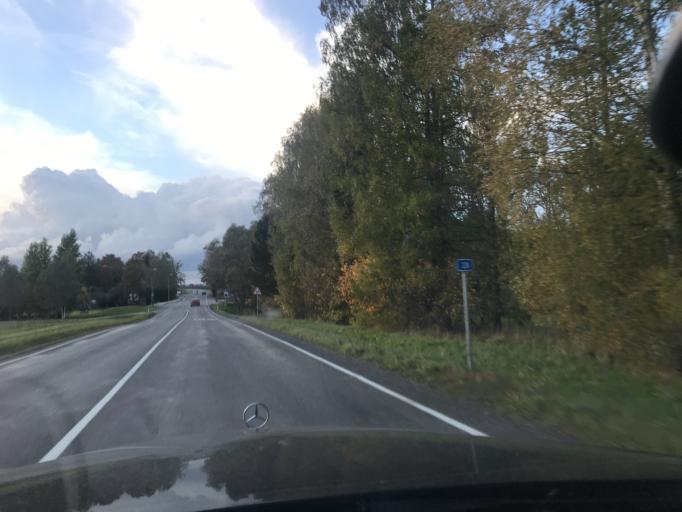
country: EE
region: Vorumaa
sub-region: Antsla vald
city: Vana-Antsla
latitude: 57.8913
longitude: 26.5037
